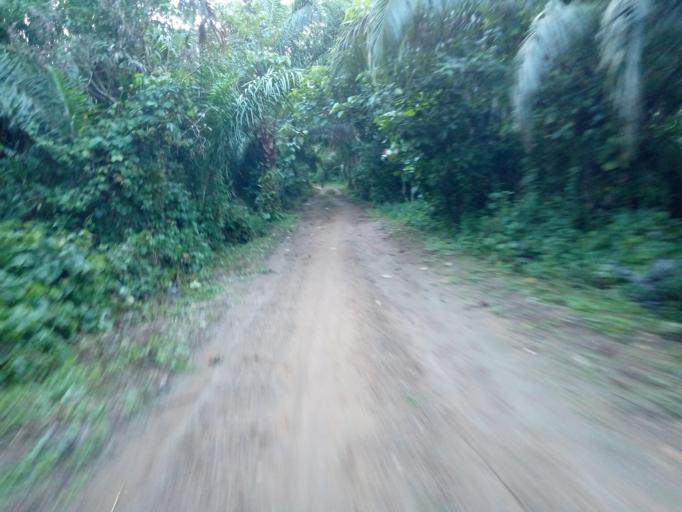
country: SL
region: Eastern Province
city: Buedu
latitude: 8.4892
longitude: -10.3417
